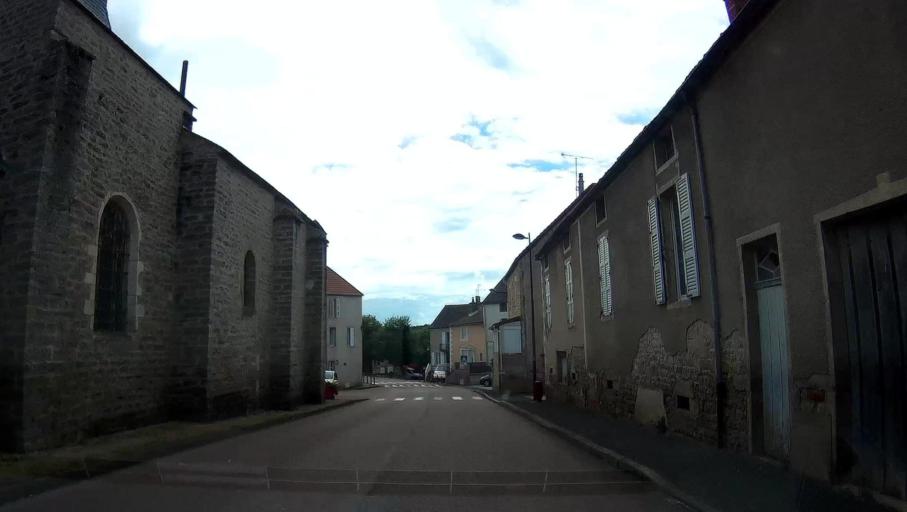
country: FR
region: Bourgogne
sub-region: Departement de Saone-et-Loire
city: Saint-Leger-sur-Dheune
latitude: 46.8666
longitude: 4.6495
